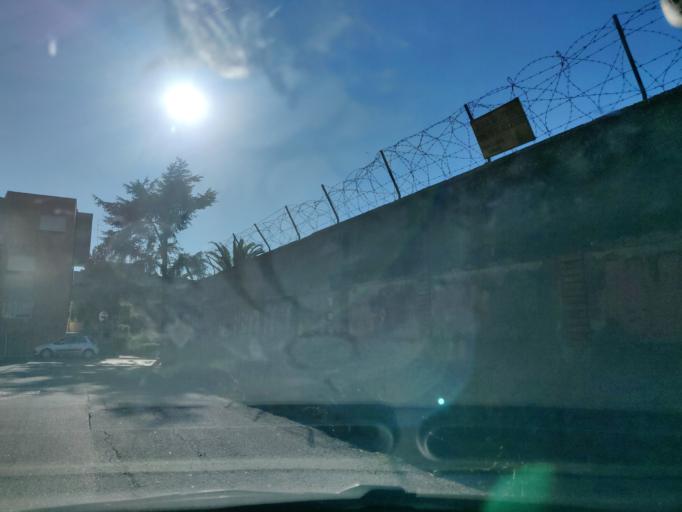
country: IT
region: Latium
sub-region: Citta metropolitana di Roma Capitale
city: Civitavecchia
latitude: 42.0876
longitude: 11.8099
